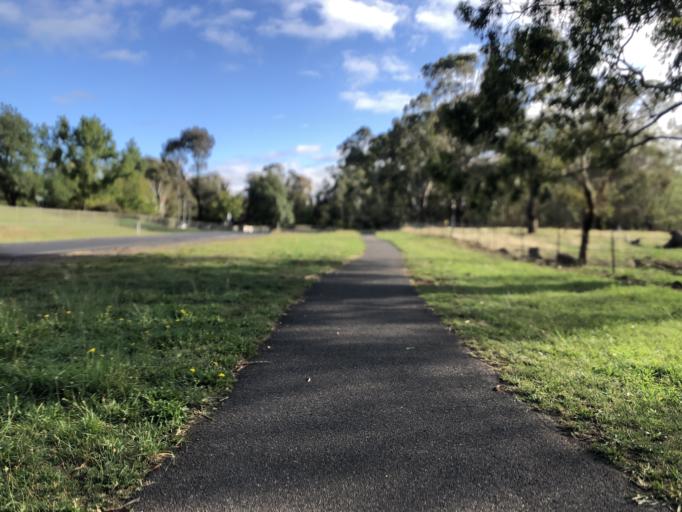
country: AU
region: New South Wales
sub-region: Orange Municipality
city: Orange
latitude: -33.3231
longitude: 149.0862
